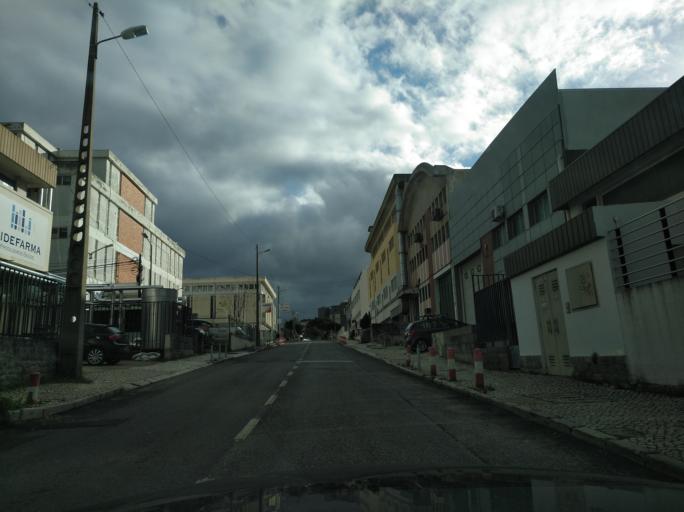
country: PT
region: Lisbon
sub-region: Loures
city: Sacavem
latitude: 38.7888
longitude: -9.1203
